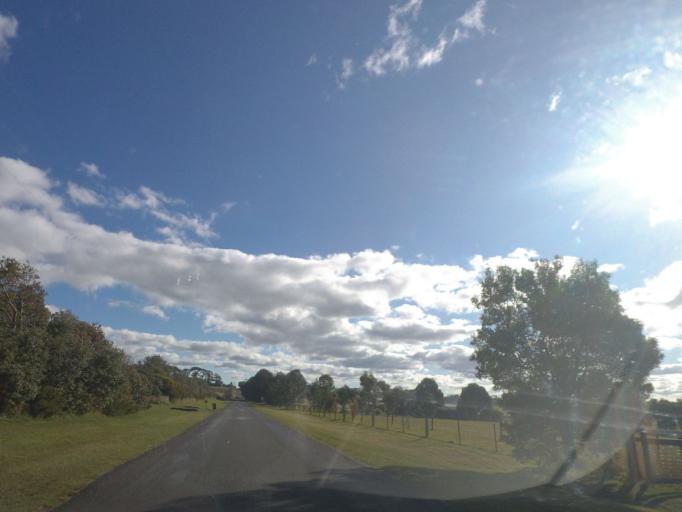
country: AU
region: Victoria
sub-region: Mount Alexander
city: Castlemaine
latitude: -37.2537
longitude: 144.4217
